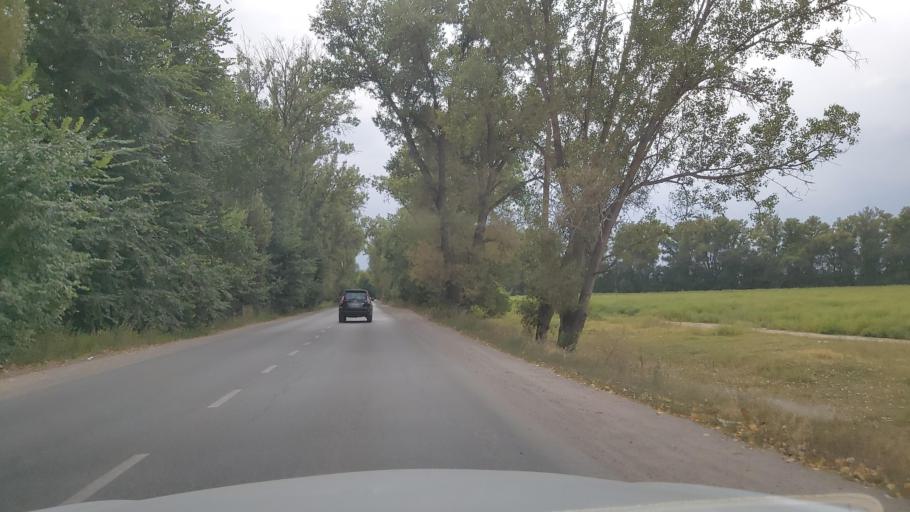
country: KZ
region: Almaty Oblysy
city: Energeticheskiy
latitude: 43.4065
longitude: 77.0558
